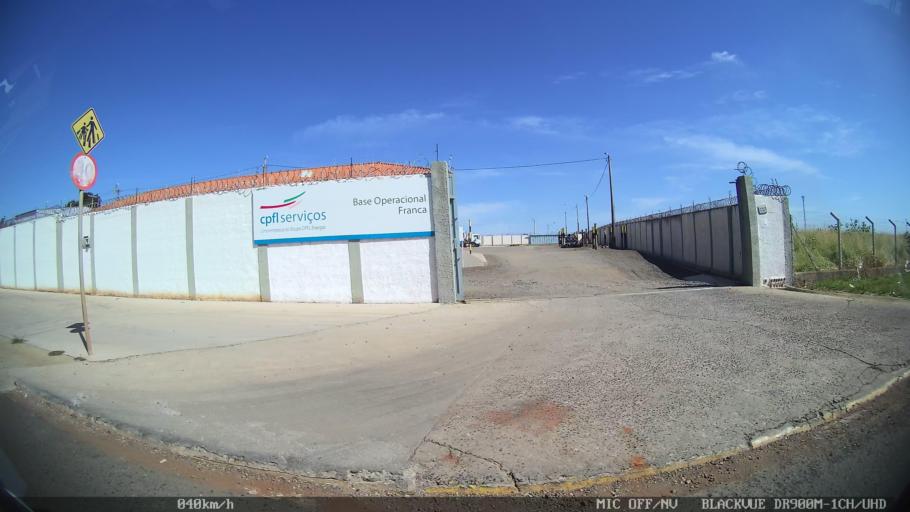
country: BR
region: Sao Paulo
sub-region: Franca
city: Franca
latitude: -20.5419
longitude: -47.4599
